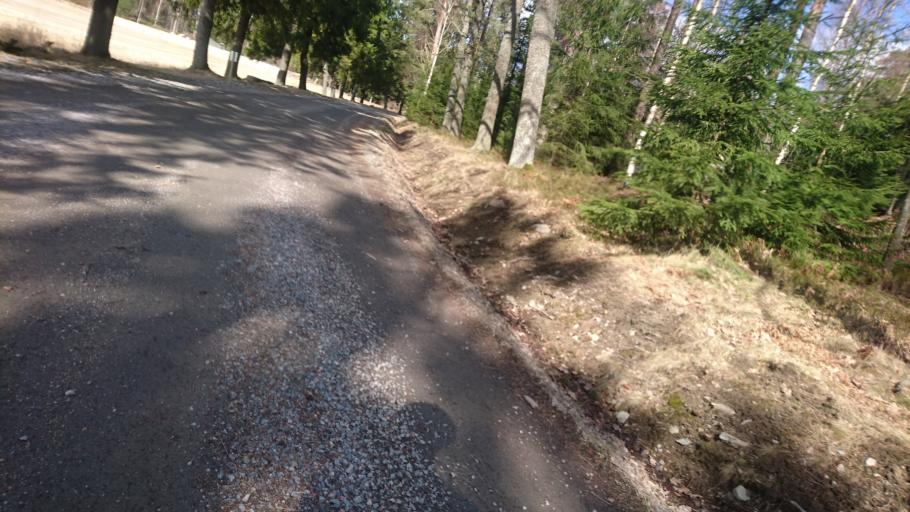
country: FI
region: Uusimaa
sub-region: Helsinki
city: Kauniainen
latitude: 60.1951
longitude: 24.7349
